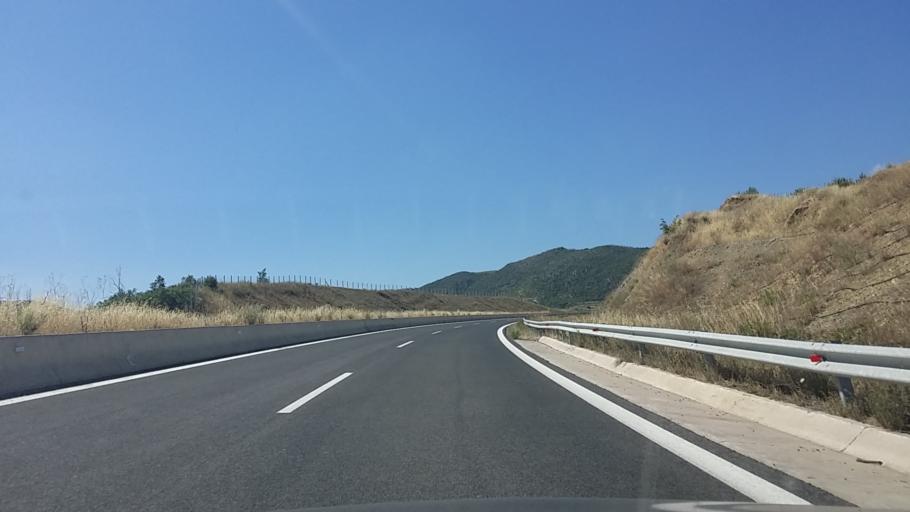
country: GR
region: Peloponnese
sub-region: Nomos Arkadias
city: Megalopoli
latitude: 37.3173
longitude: 22.1711
